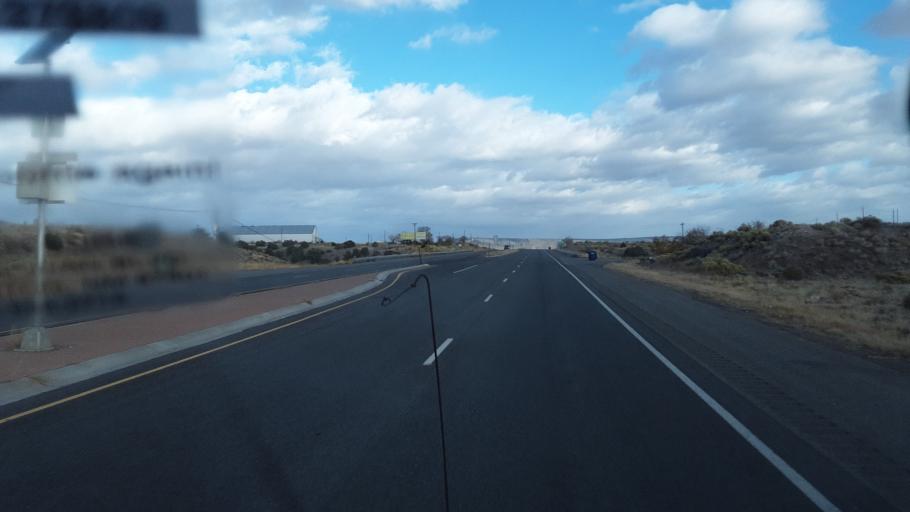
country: US
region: New Mexico
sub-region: Rio Arriba County
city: Espanola
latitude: 36.0145
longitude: -106.0891
